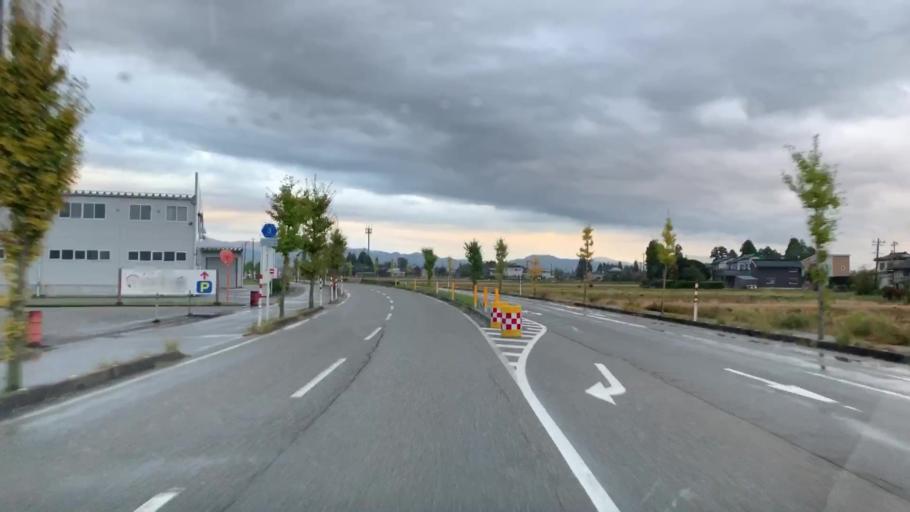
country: JP
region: Toyama
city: Kamiichi
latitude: 36.6787
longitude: 137.3275
